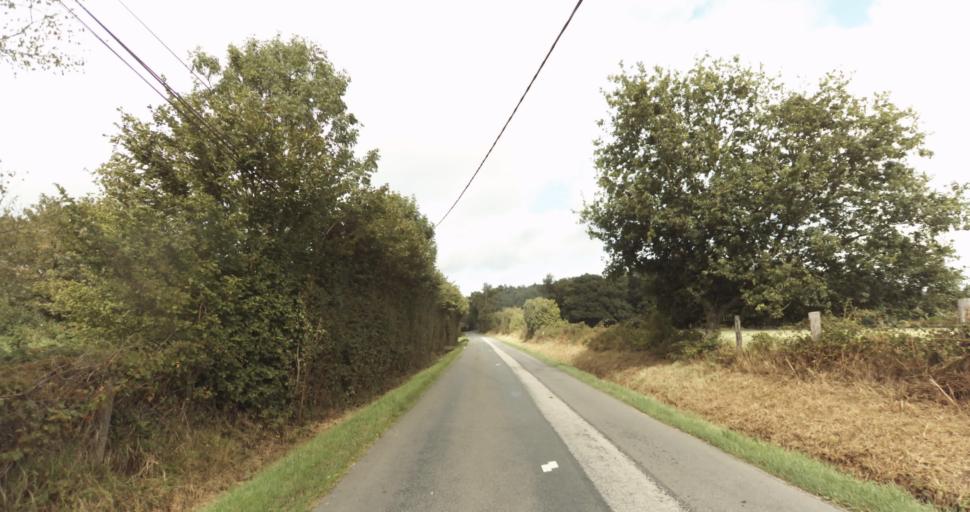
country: FR
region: Lower Normandy
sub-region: Departement de l'Orne
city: Gace
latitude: 48.8035
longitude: 0.2536
